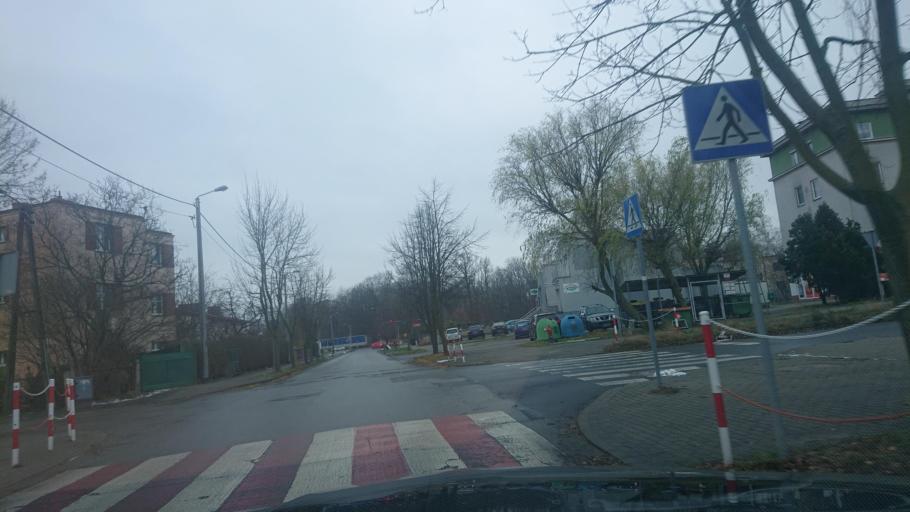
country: PL
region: Greater Poland Voivodeship
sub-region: Powiat gnieznienski
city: Gniezno
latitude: 52.5364
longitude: 17.5802
